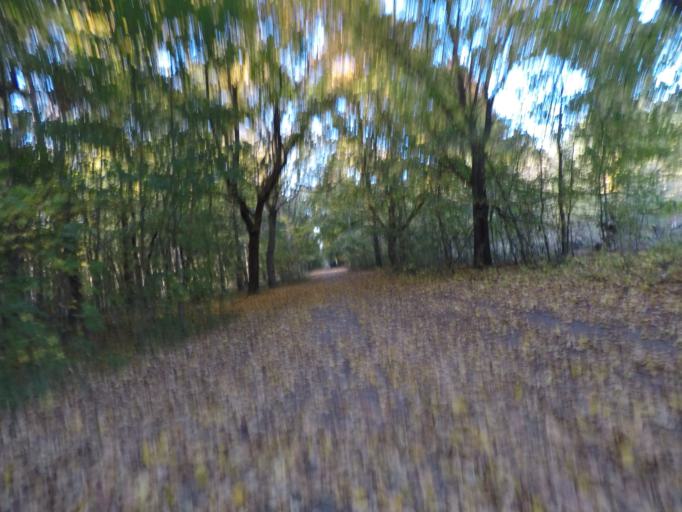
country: DE
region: Brandenburg
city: Biesenthal
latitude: 52.7802
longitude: 13.6404
